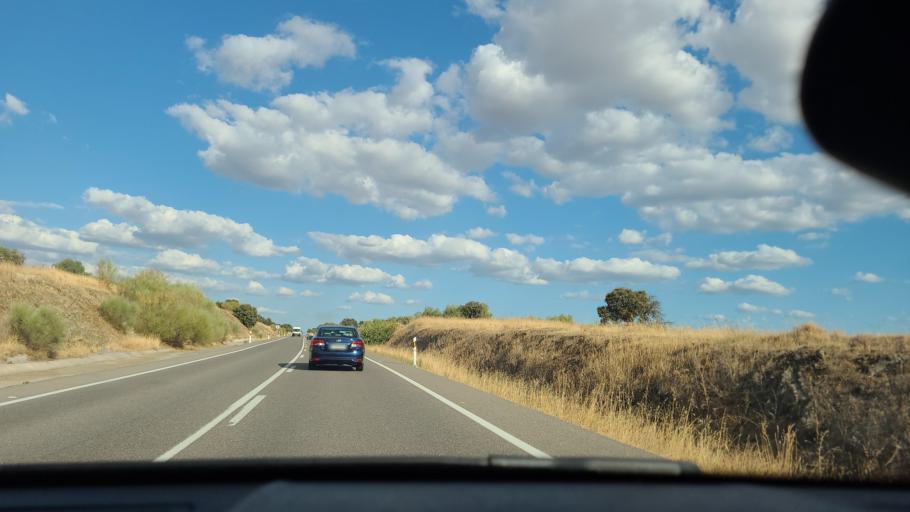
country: ES
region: Andalusia
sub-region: Province of Cordoba
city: Fuente Obejuna
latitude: 38.2656
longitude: -5.4999
